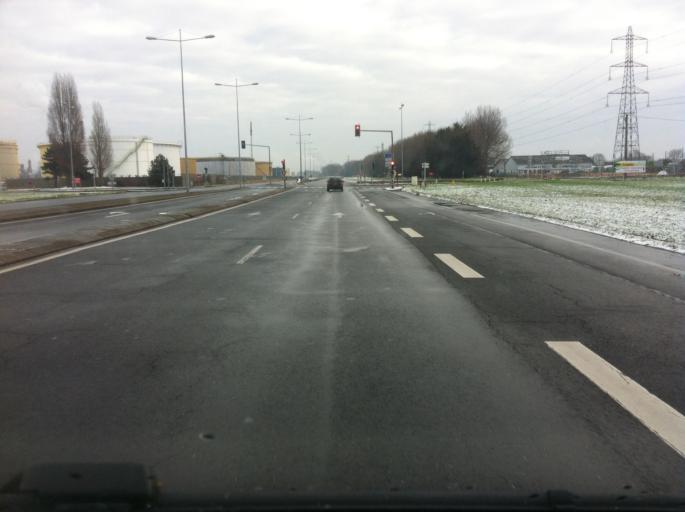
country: FR
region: Haute-Normandie
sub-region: Departement de la Seine-Maritime
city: Harfleur
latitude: 49.4855
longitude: 0.2231
